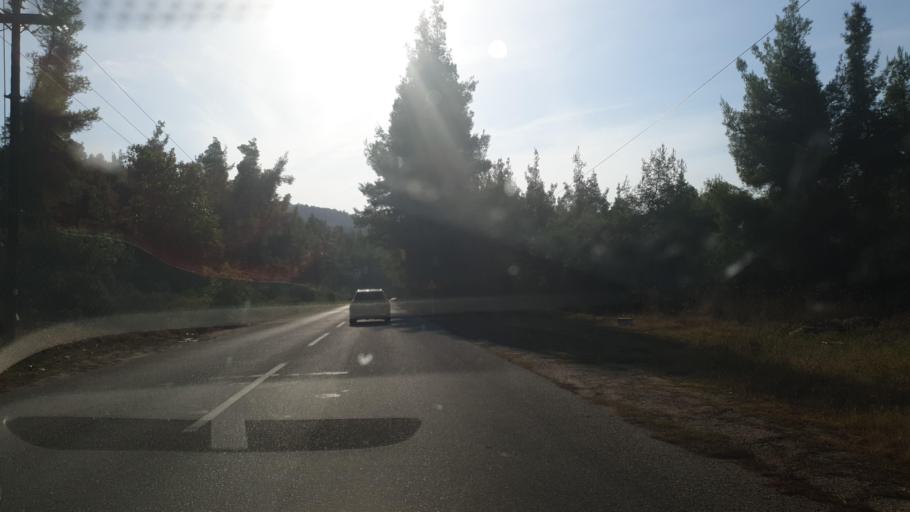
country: GR
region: Central Macedonia
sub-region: Nomos Chalkidikis
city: Neos Marmaras
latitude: 40.1794
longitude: 23.8212
